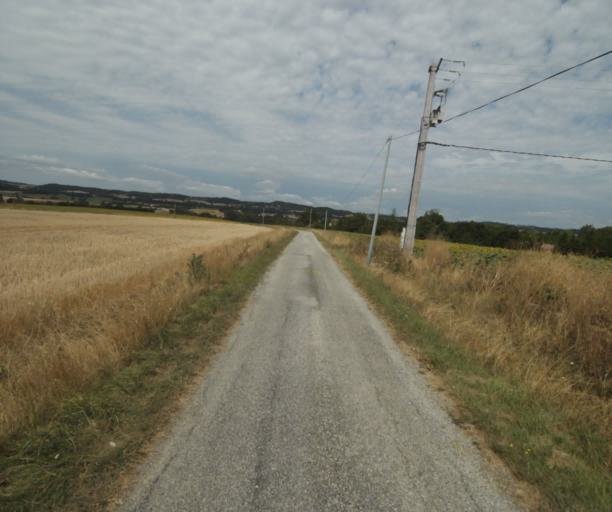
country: FR
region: Midi-Pyrenees
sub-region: Departement de la Haute-Garonne
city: Saint-Felix-Lauragais
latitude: 43.3972
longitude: 1.9055
